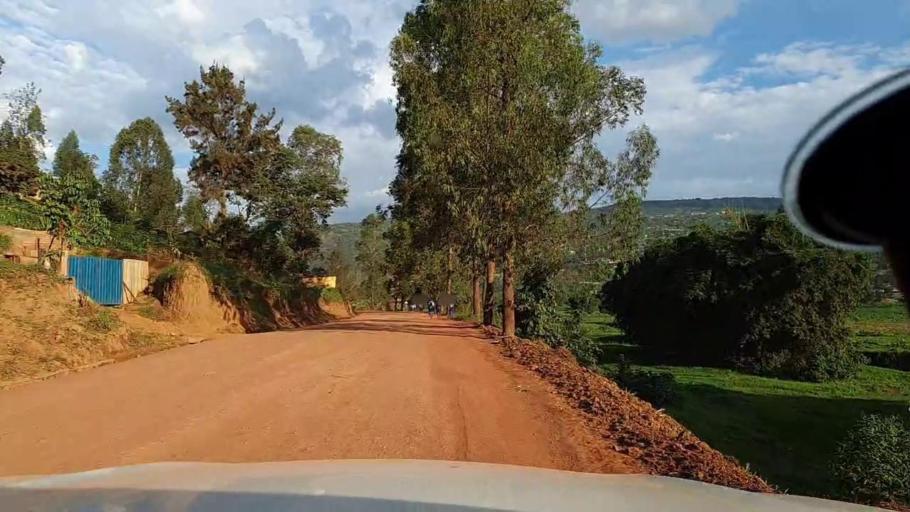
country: RW
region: Kigali
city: Kigali
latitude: -1.9459
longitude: 30.0115
